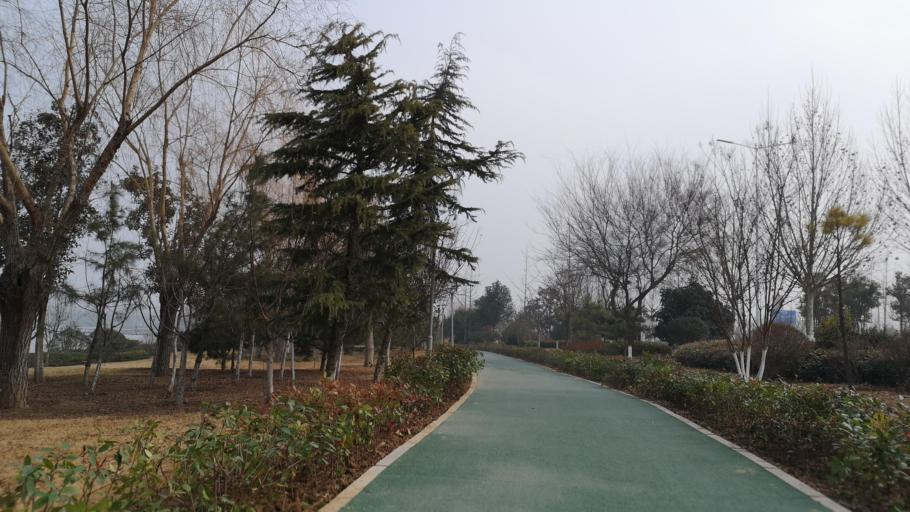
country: CN
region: Henan Sheng
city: Zhongyuanlu
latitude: 35.8001
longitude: 115.0539
